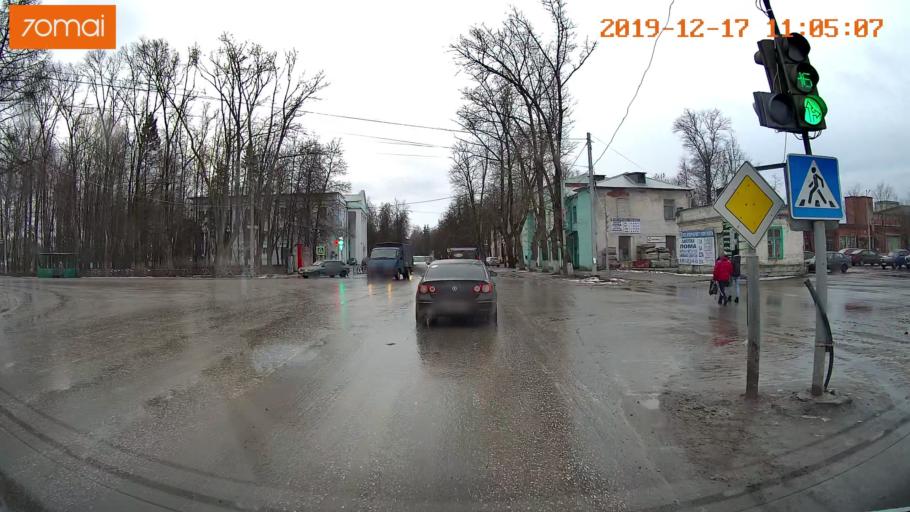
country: RU
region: Vladimir
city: Gus'-Khrustal'nyy
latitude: 55.6225
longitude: 40.6434
